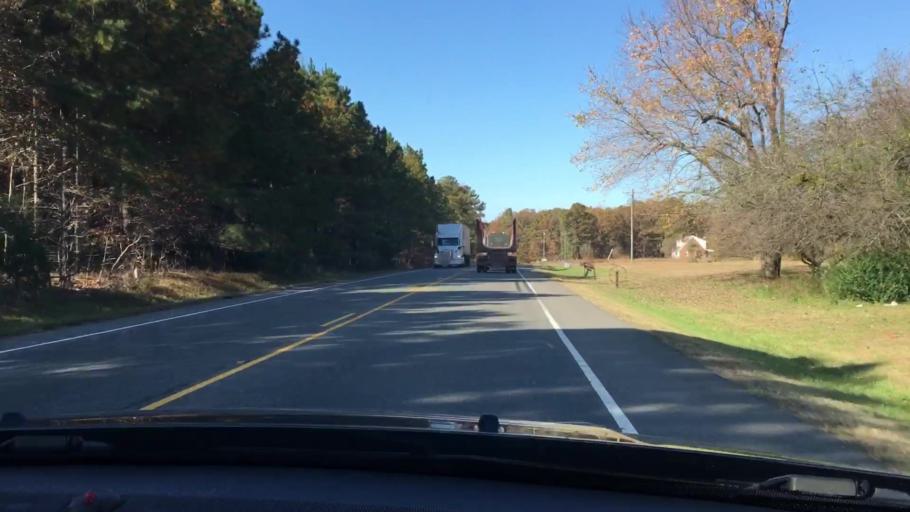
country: US
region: Virginia
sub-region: King William County
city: Central Garage
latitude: 37.7693
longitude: -77.1541
